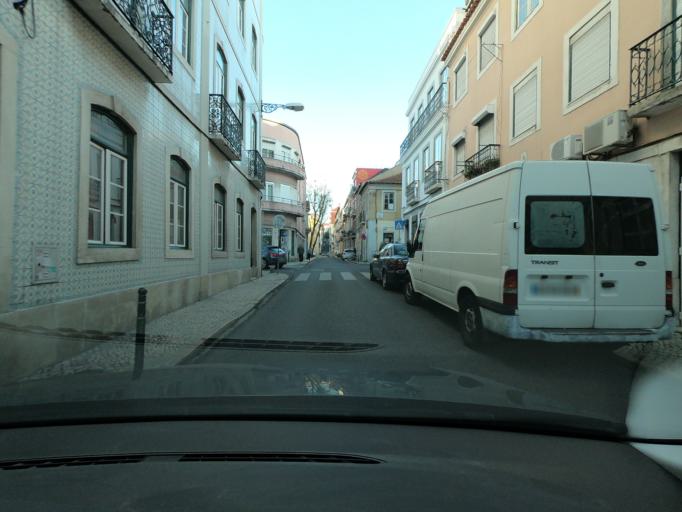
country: PT
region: Lisbon
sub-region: Lisbon
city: Lisbon
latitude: 38.7190
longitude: -9.1279
